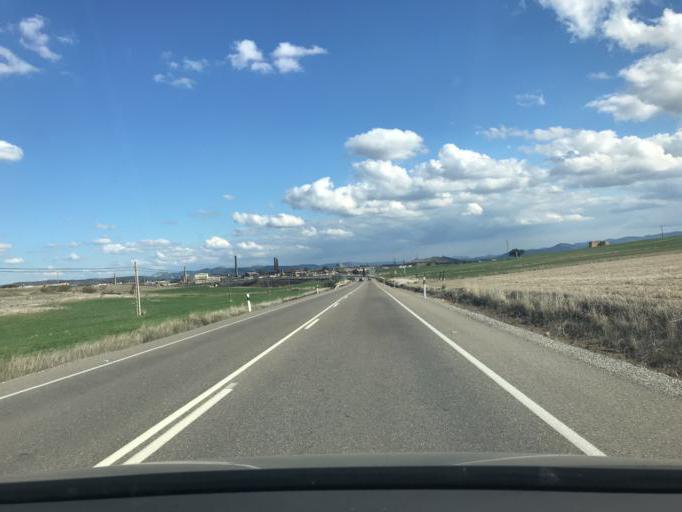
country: ES
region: Andalusia
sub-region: Province of Cordoba
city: Penarroya-Pueblonuevo
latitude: 38.2960
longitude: -5.2891
